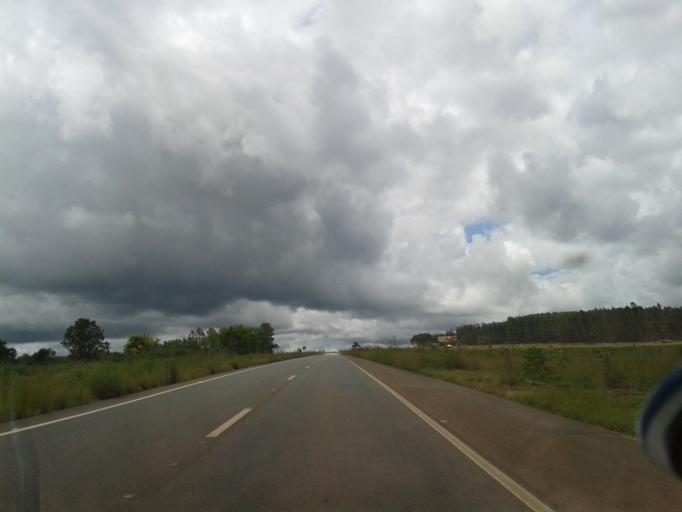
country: BR
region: Goias
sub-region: Goias
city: Goias
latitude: -16.0040
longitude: -50.0167
